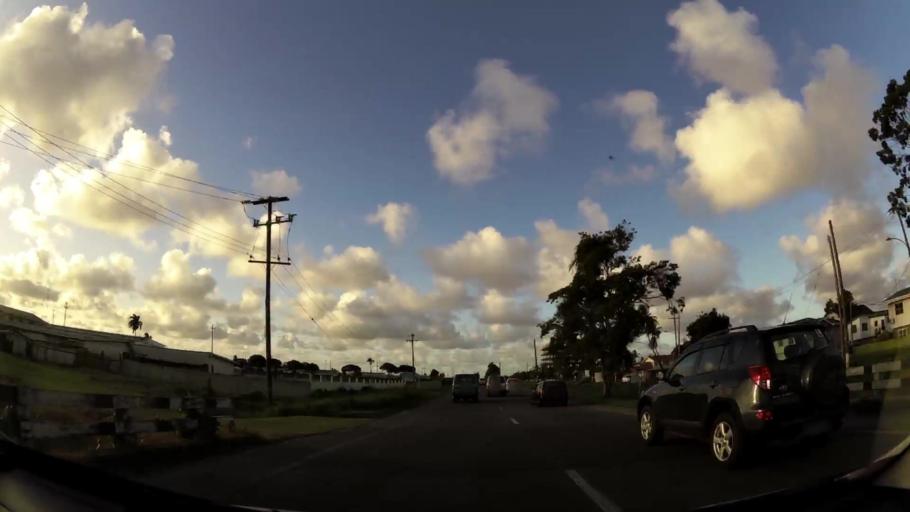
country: GY
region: Demerara-Mahaica
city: Georgetown
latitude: 6.8158
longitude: -58.1460
